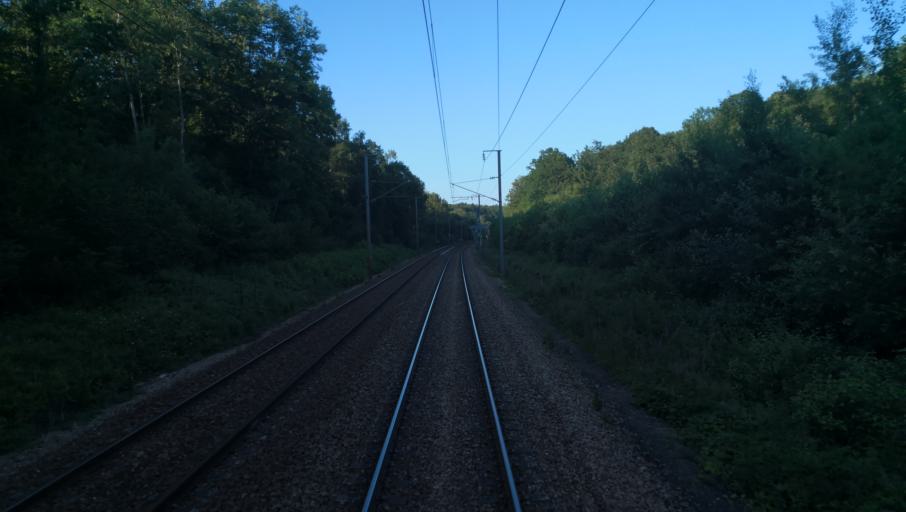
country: FR
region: Haute-Normandie
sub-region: Departement de l'Eure
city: Bernay
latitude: 49.0900
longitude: 0.5271
